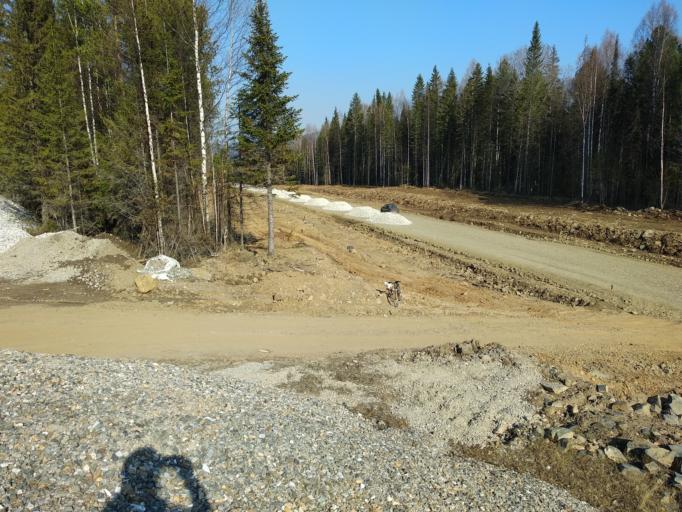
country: RU
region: Sverdlovsk
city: Karpinsk
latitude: 59.5262
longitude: 59.2399
